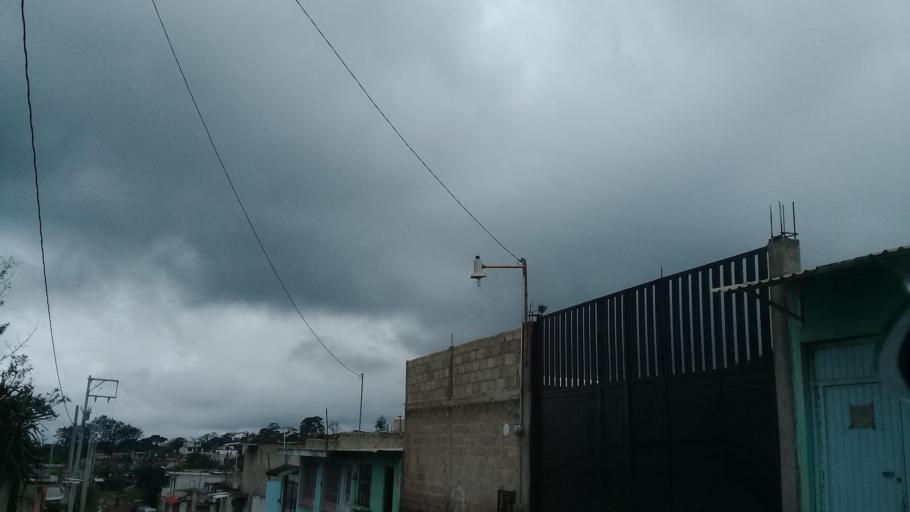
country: MX
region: Veracruz
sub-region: Emiliano Zapata
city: Las Trancas
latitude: 19.4972
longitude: -96.8655
